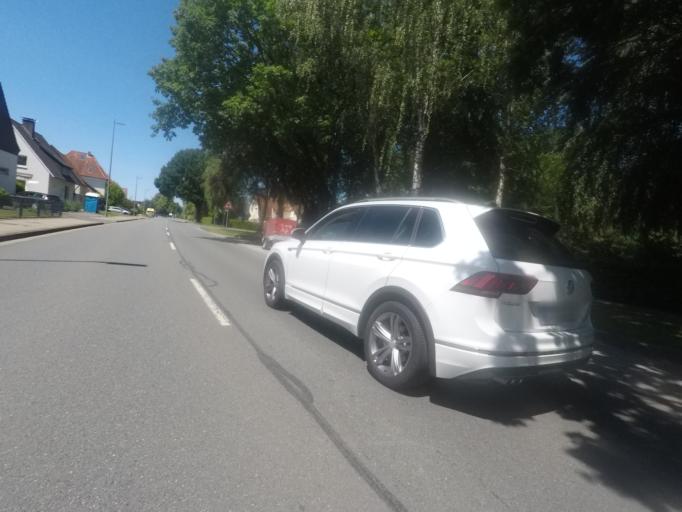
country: DE
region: North Rhine-Westphalia
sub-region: Regierungsbezirk Detmold
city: Bielefeld
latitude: 52.0693
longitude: 8.5209
